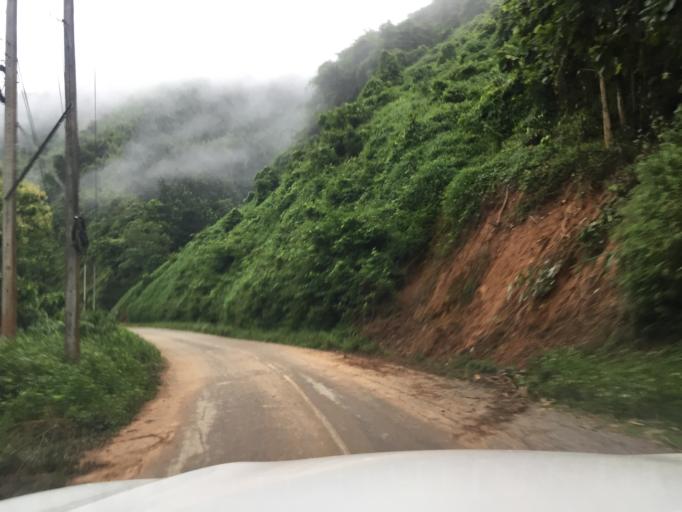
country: LA
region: Phongsali
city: Khoa
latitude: 21.0755
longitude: 102.3774
